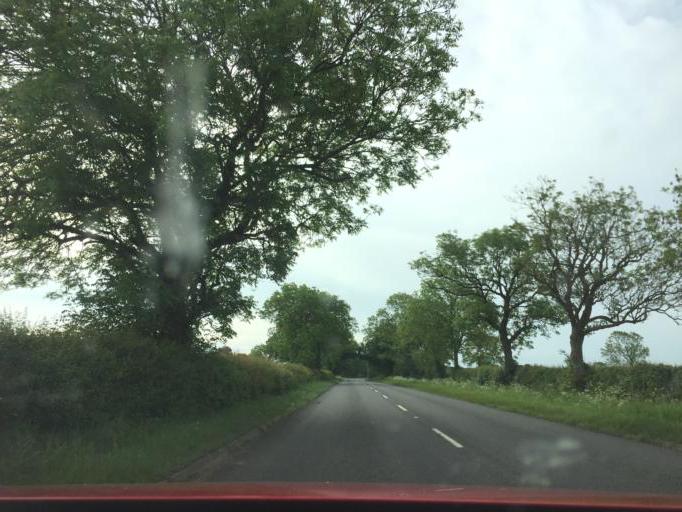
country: GB
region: England
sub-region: Leicestershire
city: Hinckley
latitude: 52.4807
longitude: -1.3322
